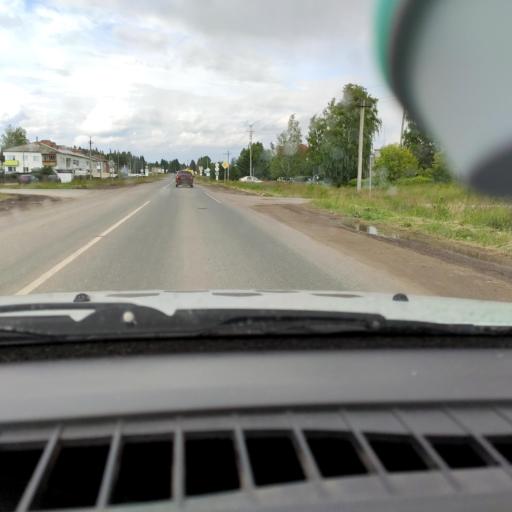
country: RU
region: Perm
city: Orda
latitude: 57.1976
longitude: 56.9099
